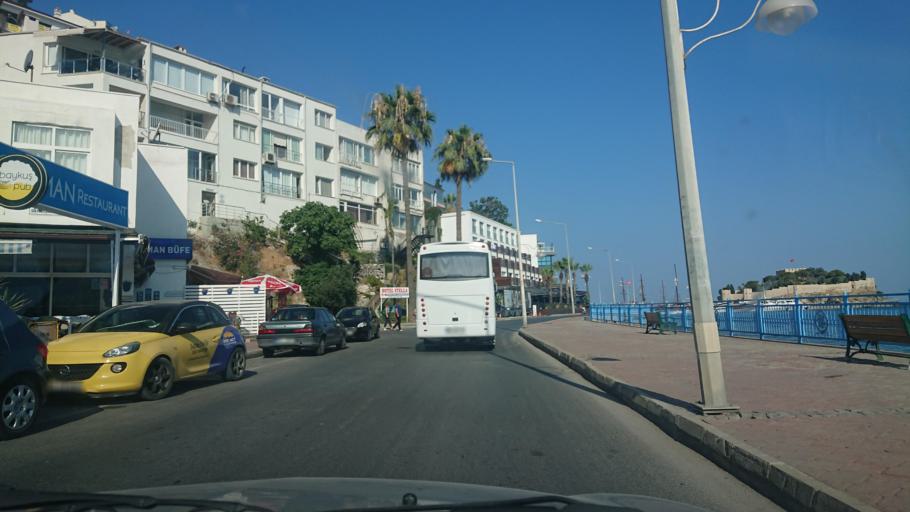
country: TR
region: Aydin
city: Kusadasi
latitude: 37.8609
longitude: 27.2531
